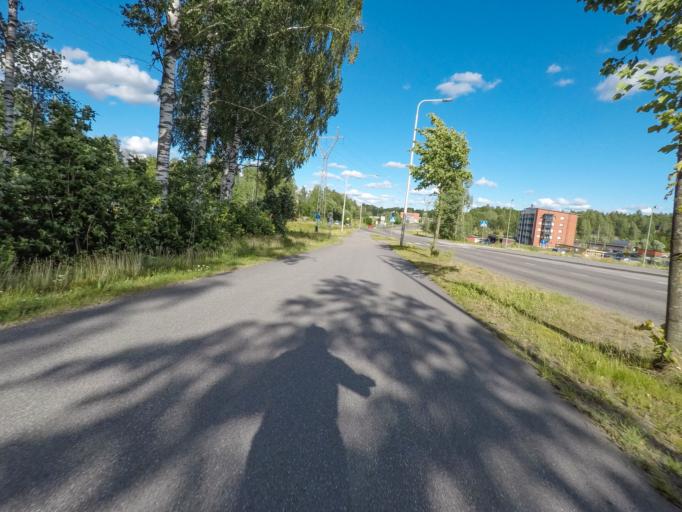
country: FI
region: South Karelia
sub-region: Lappeenranta
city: Lappeenranta
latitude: 61.0649
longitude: 28.1637
